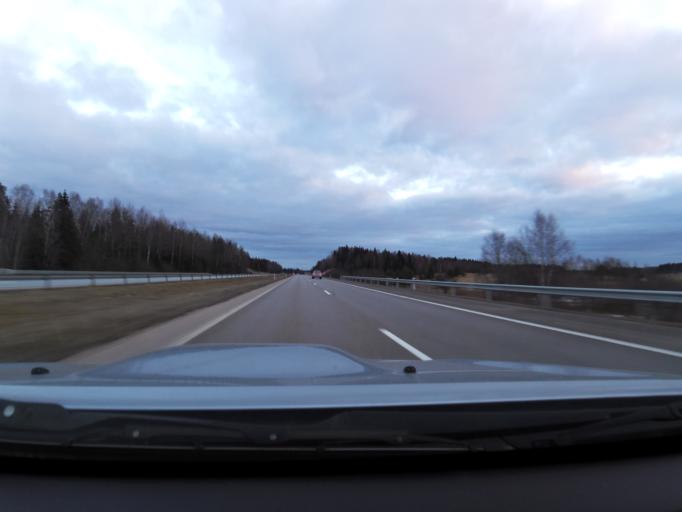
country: LT
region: Vilnius County
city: Pasilaiciai
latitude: 54.8207
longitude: 25.1387
